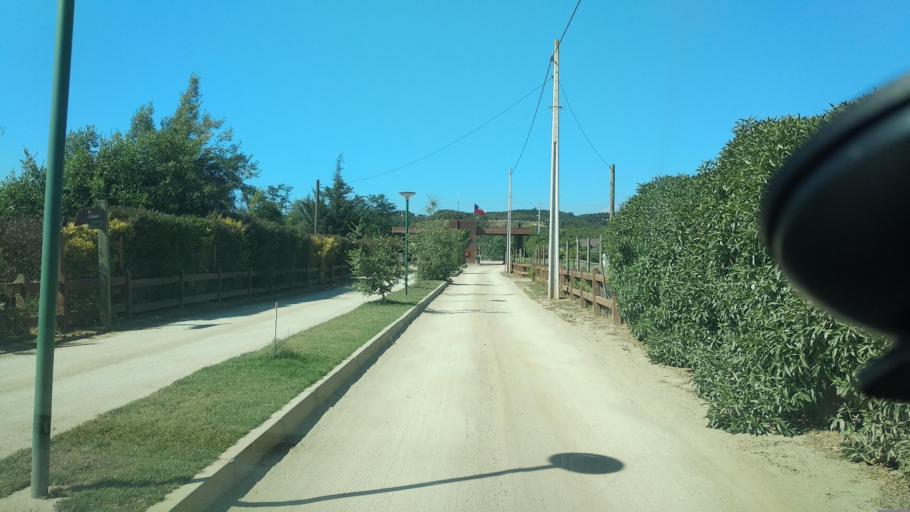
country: CL
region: Valparaiso
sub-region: Provincia de Marga Marga
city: Limache
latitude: -32.9705
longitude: -71.3079
